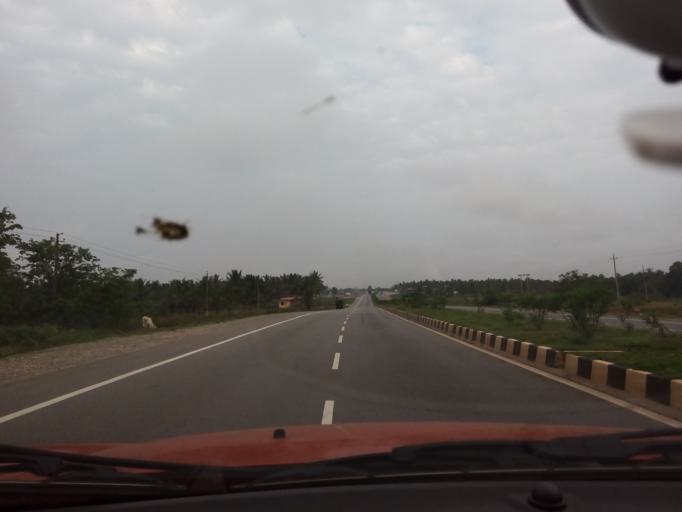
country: IN
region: Karnataka
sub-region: Mandya
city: Belluru
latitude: 12.9586
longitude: 76.5992
